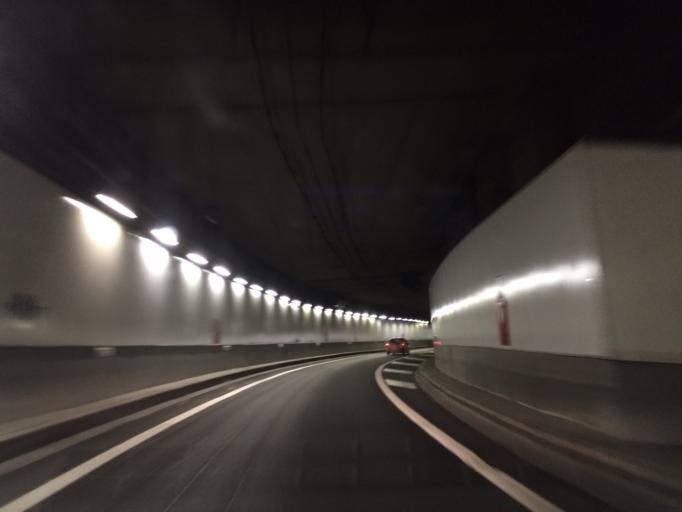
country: ES
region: Madrid
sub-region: Provincia de Madrid
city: Moncloa-Aravaca
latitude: 40.4197
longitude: -3.7223
